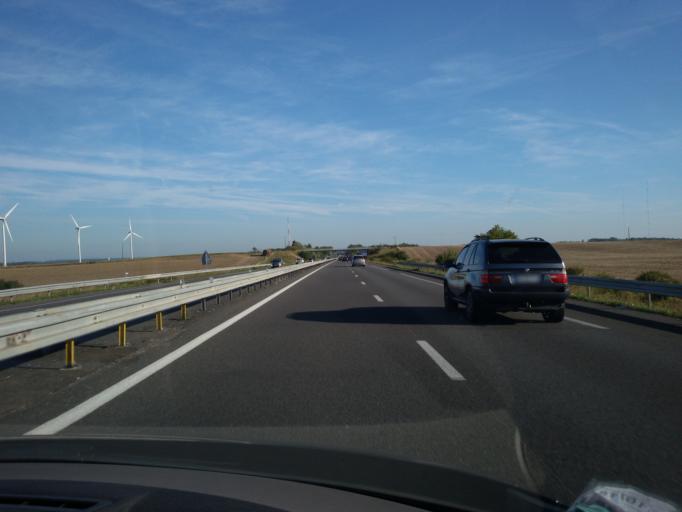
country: FR
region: Centre
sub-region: Departement du Cher
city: Mehun-sur-Yevre
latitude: 47.1343
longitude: 2.1877
